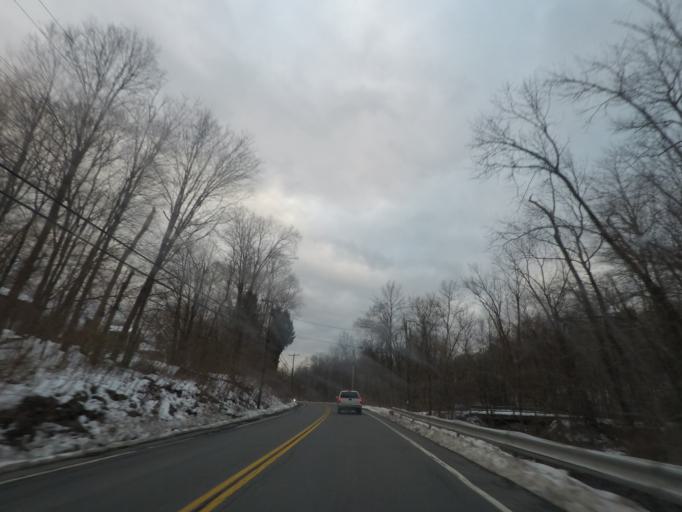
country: US
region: New York
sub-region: Orange County
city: Balmville
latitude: 41.5335
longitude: -74.0388
